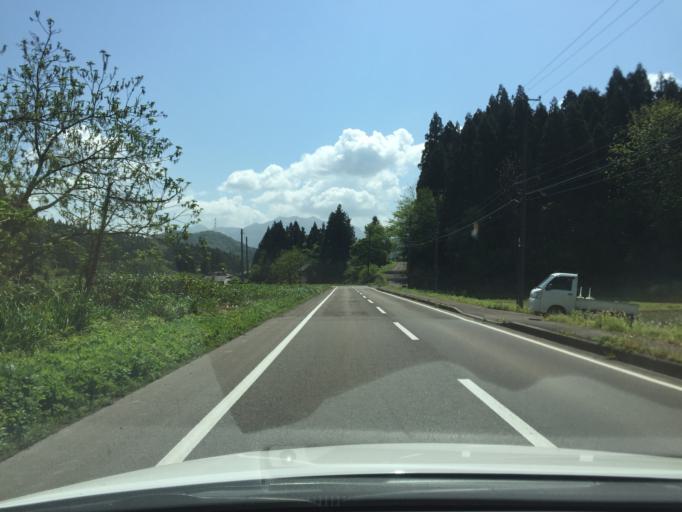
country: JP
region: Niigata
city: Kamo
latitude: 37.5769
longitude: 139.0778
